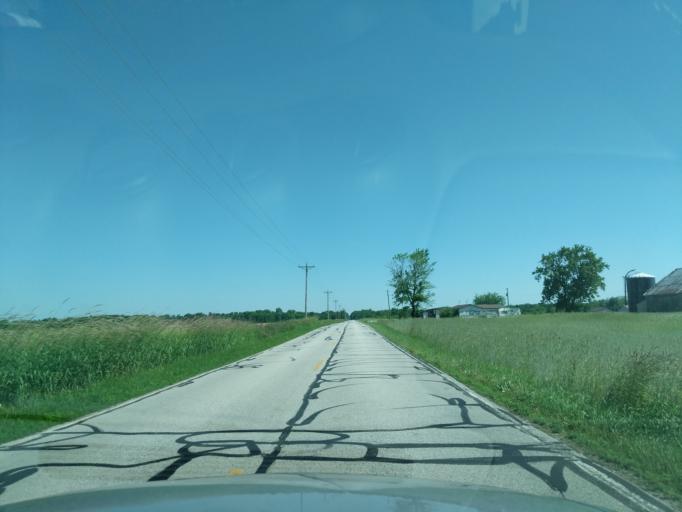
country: US
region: Indiana
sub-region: Huntington County
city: Warren
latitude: 40.7065
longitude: -85.5070
